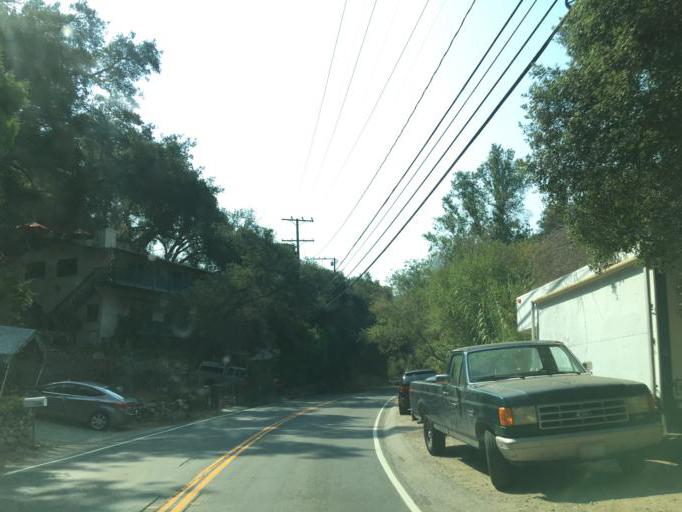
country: US
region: California
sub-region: Los Angeles County
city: Topanga
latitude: 34.0991
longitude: -118.6176
